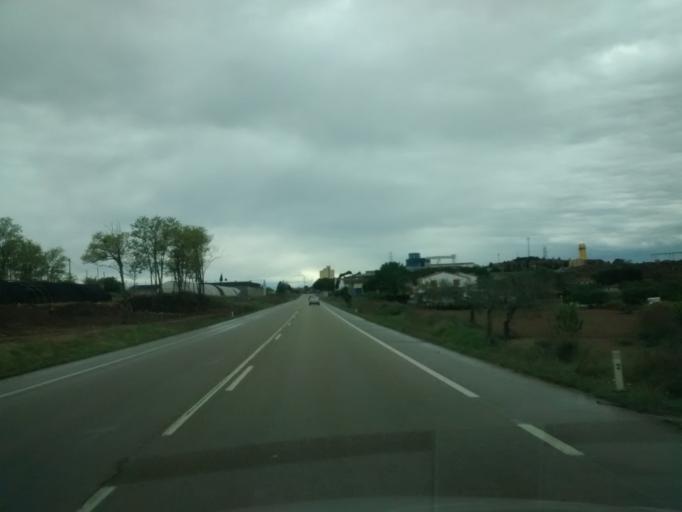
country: ES
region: Aragon
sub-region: Provincia de Zaragoza
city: Caspe
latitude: 41.2229
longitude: -0.0224
